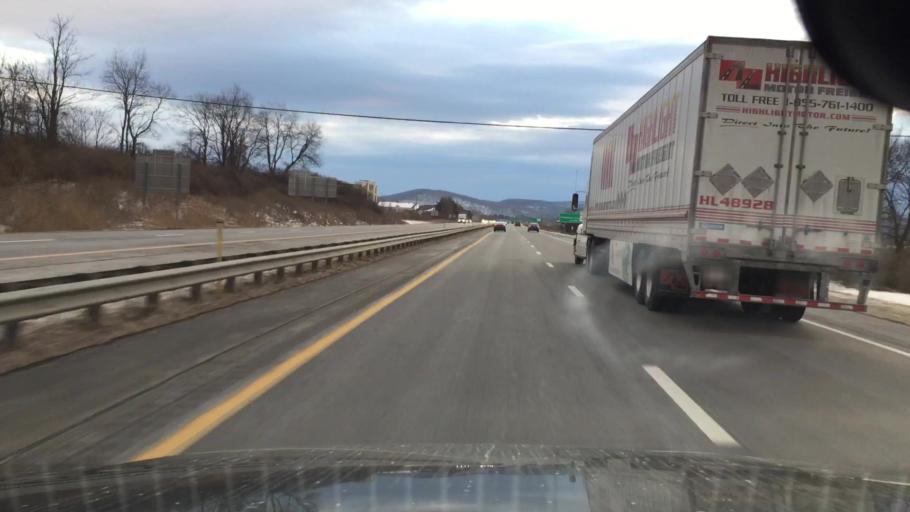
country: US
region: New York
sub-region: Chemung County
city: Horseheads
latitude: 42.1596
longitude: -76.8668
